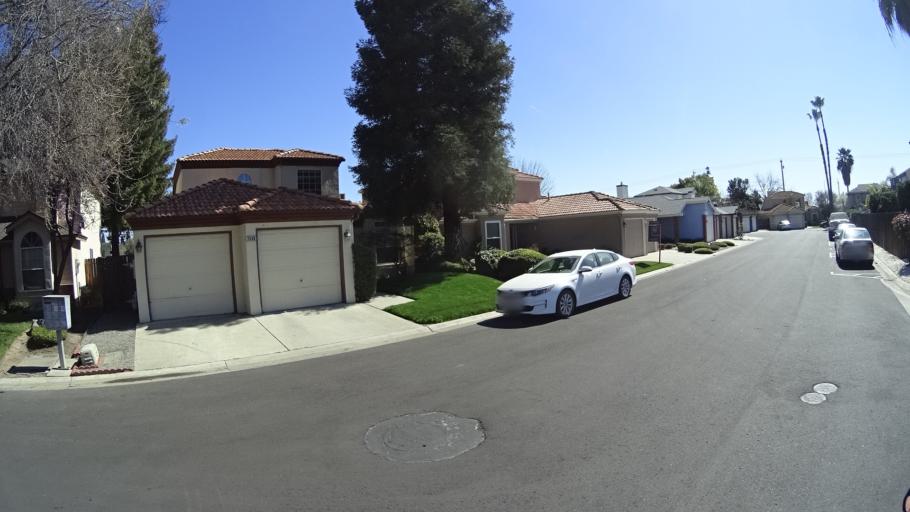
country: US
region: California
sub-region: Fresno County
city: Clovis
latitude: 36.8458
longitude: -119.7594
